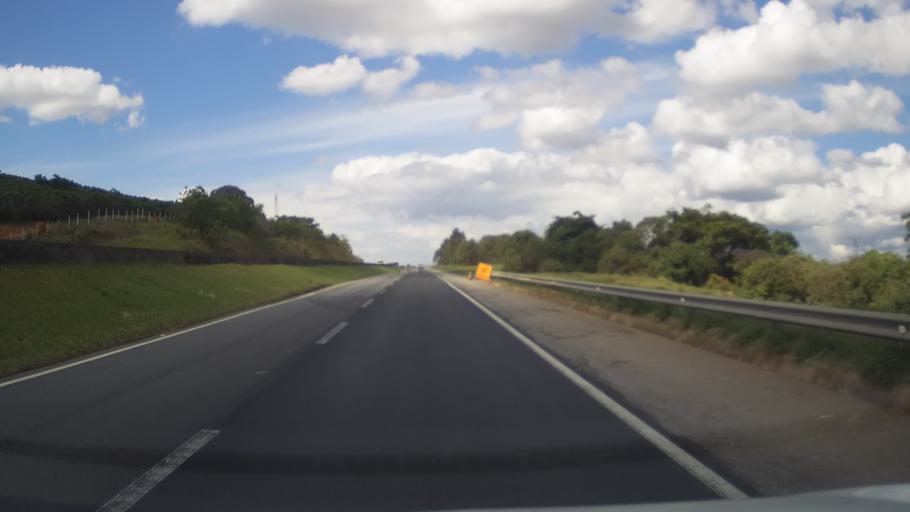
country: BR
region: Minas Gerais
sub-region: Santo Antonio Do Amparo
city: Santo Antonio do Amparo
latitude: -20.8423
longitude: -44.8269
